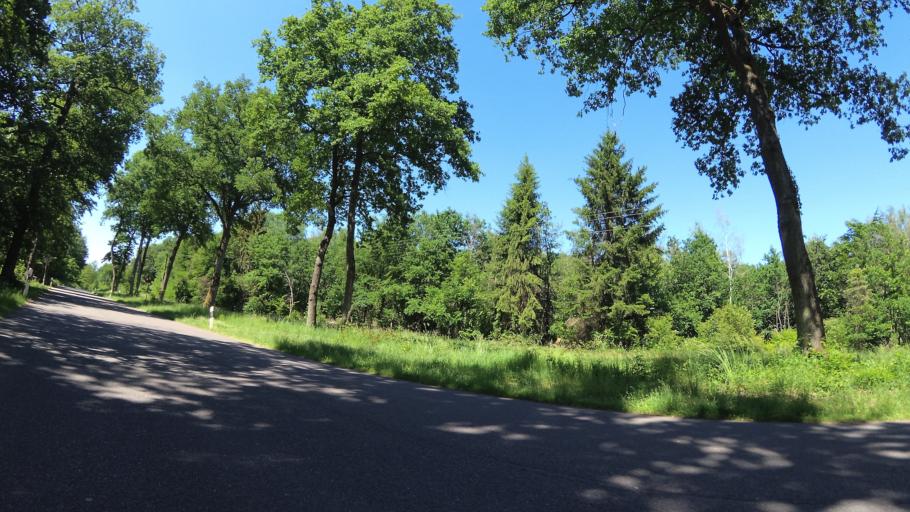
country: DE
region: Saarland
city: Saarwellingen
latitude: 49.3599
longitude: 6.7910
